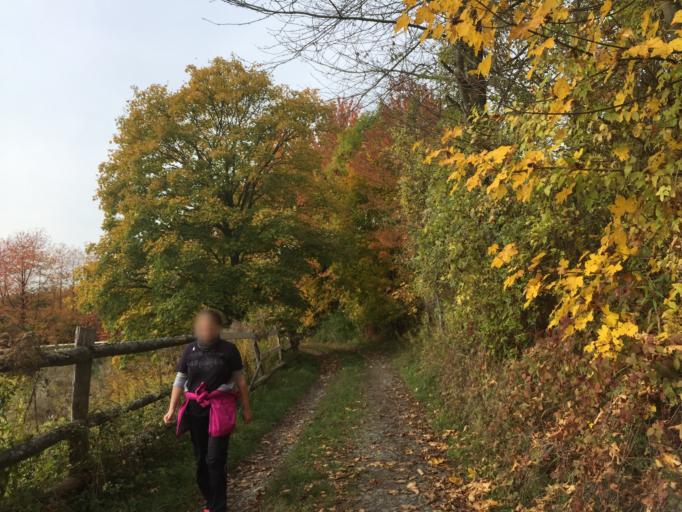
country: DE
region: Hesse
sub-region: Regierungsbezirk Darmstadt
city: Bensheim
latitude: 49.7023
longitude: 8.6508
